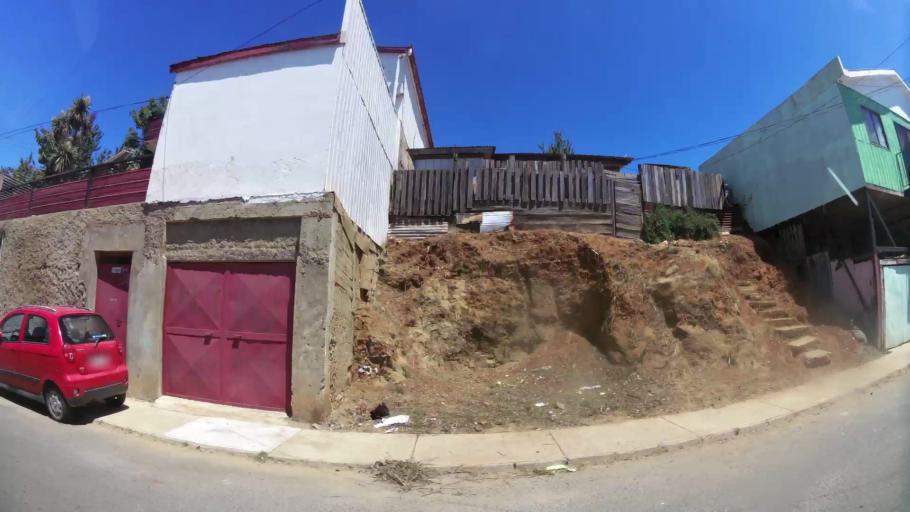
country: CL
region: Valparaiso
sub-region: Provincia de Valparaiso
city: Valparaiso
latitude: -33.0539
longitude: -71.6408
